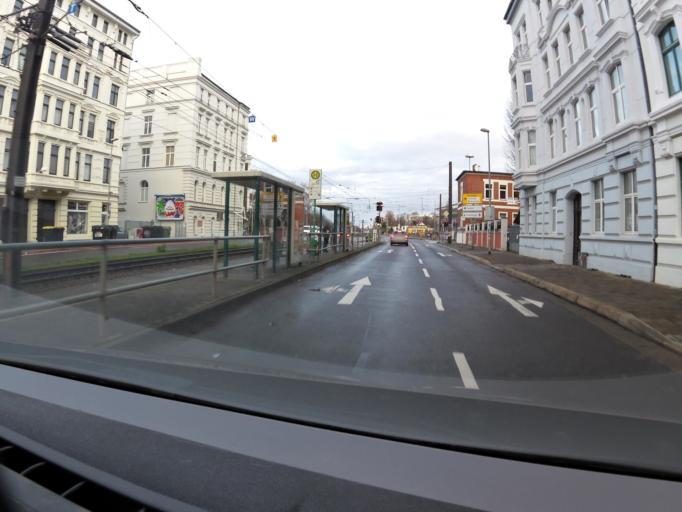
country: DE
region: Saxony-Anhalt
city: Magdeburg
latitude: 52.1290
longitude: 11.6055
